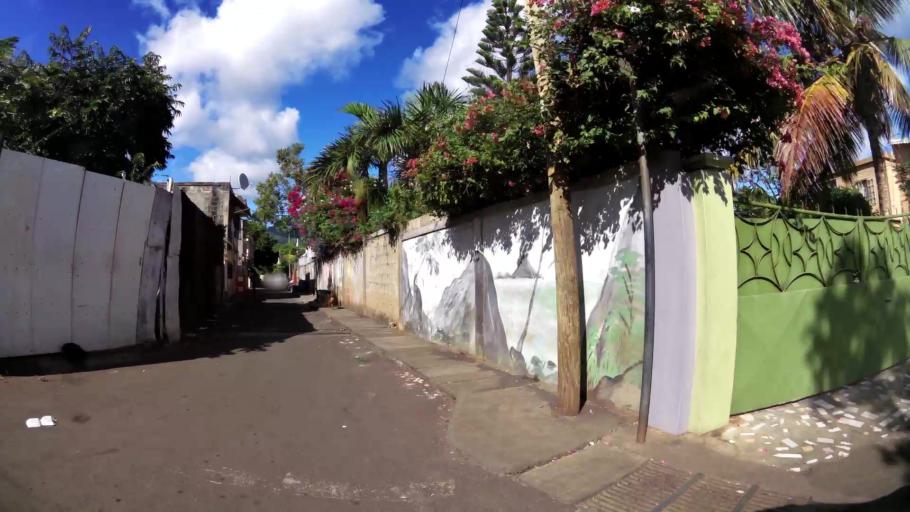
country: MU
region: Pamplemousses
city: Le Hochet
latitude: -20.1435
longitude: 57.5162
